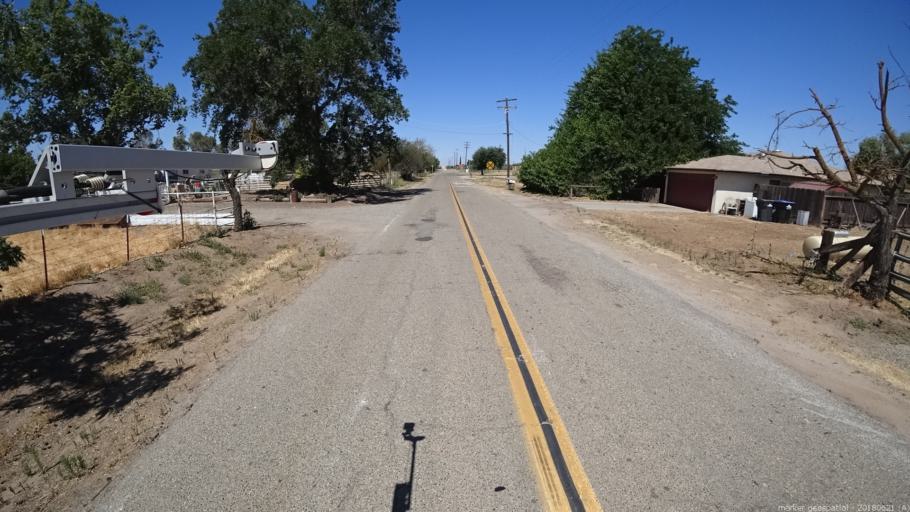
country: US
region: California
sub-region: Madera County
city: Parksdale
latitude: 36.9094
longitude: -119.9588
